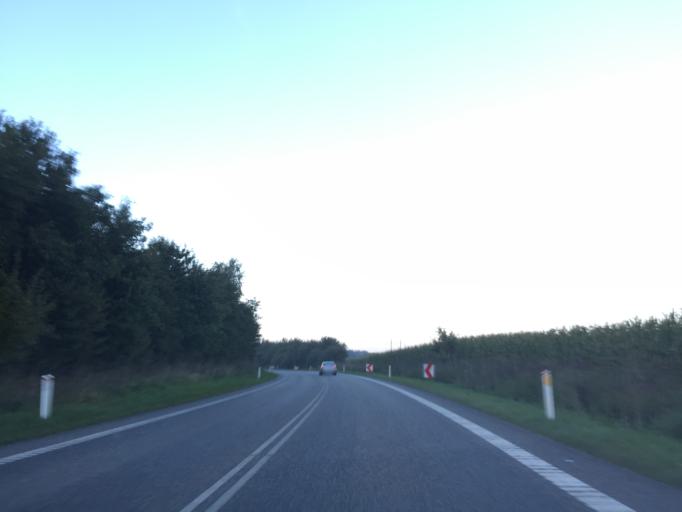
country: DK
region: South Denmark
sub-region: Aabenraa Kommune
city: Lojt Kirkeby
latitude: 55.0948
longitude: 9.4349
